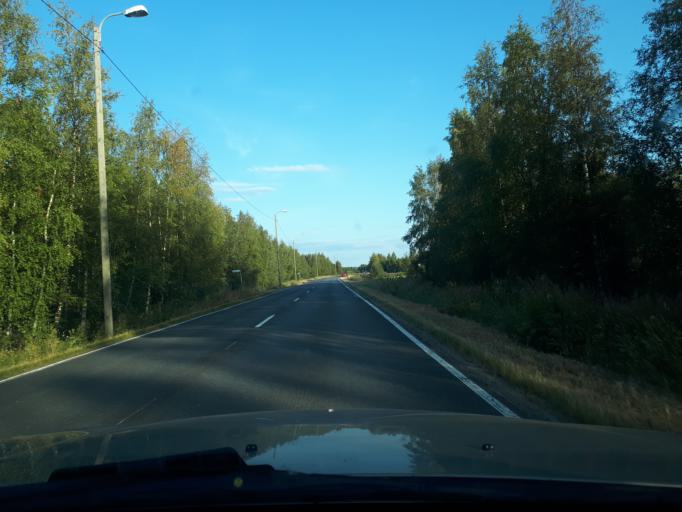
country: FI
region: Northern Ostrobothnia
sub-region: Oulu
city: Oulunsalo
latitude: 64.9841
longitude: 25.2669
